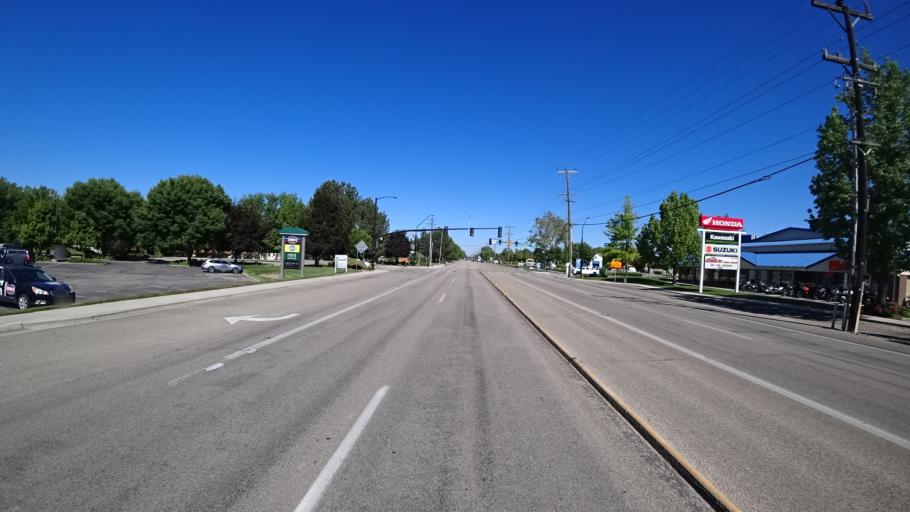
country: US
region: Idaho
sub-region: Ada County
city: Garden City
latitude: 43.6553
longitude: -116.2579
